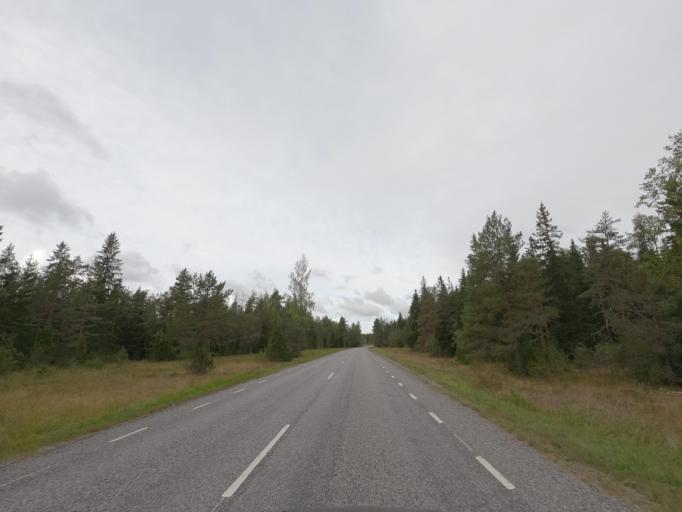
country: EE
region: Raplamaa
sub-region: Rapla vald
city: Rapla
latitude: 59.0051
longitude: 24.6249
